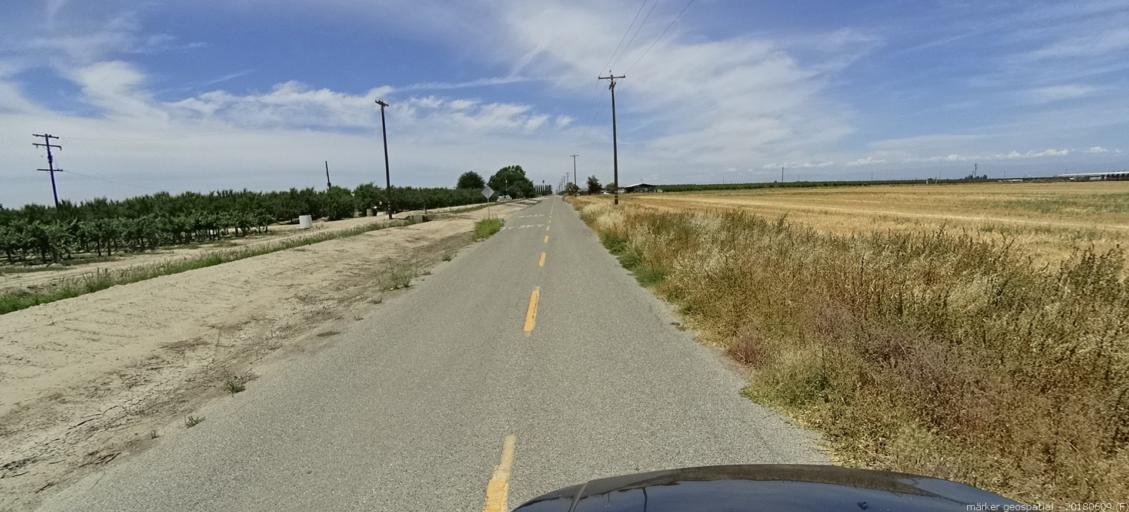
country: US
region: California
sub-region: Madera County
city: Parkwood
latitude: 36.9106
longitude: -120.1015
